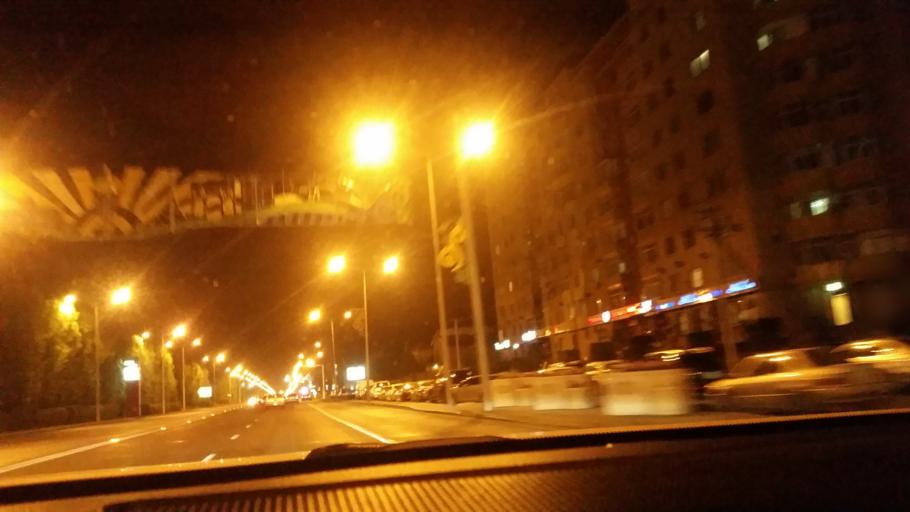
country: KZ
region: Astana Qalasy
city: Astana
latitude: 51.1417
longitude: 71.4843
